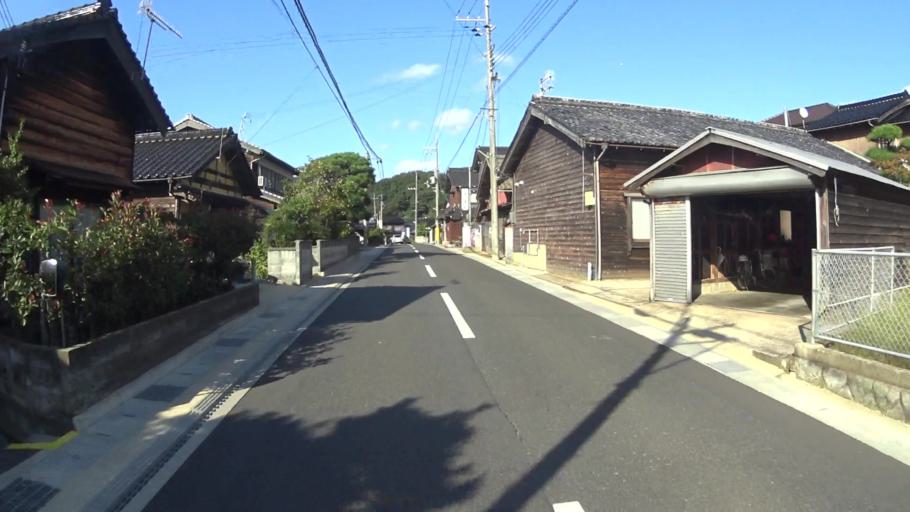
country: JP
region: Hyogo
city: Toyooka
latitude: 35.6598
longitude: 134.9680
